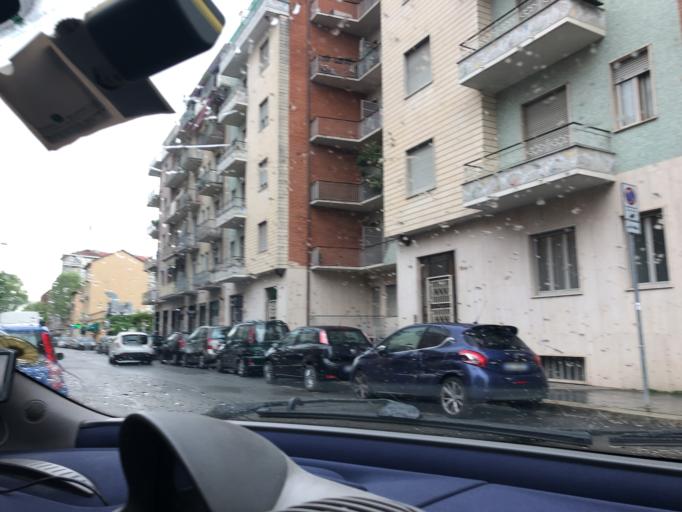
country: IT
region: Piedmont
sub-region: Provincia di Torino
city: Lesna
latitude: 45.0763
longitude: 7.6228
